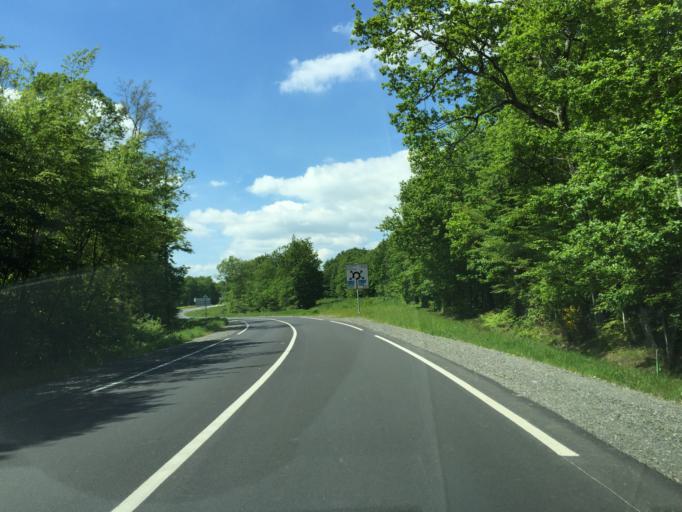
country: FR
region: Auvergne
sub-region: Departement de l'Allier
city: Brugheas
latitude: 46.0982
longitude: 3.3513
